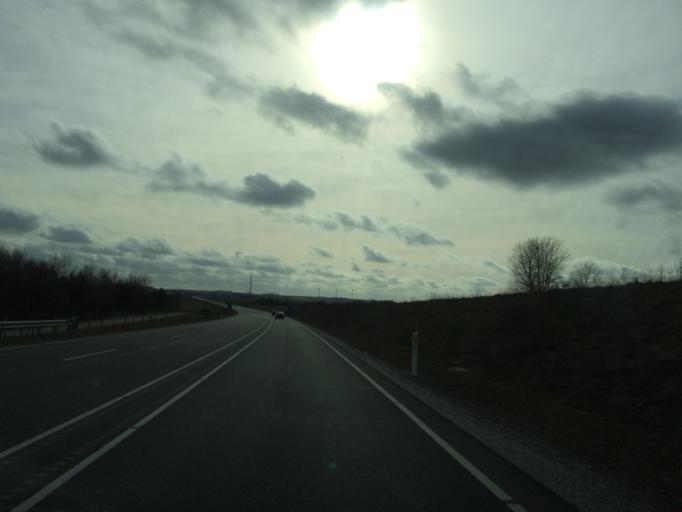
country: DK
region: Central Jutland
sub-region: Randers Kommune
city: Assentoft
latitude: 56.4287
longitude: 10.1193
